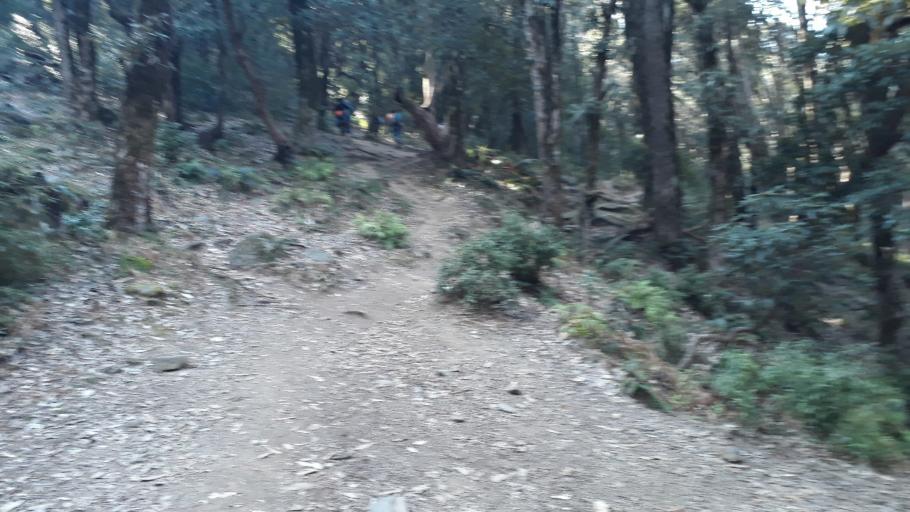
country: IN
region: Himachal Pradesh
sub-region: Mandi
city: Pandoh
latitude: 31.7689
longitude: 77.0923
